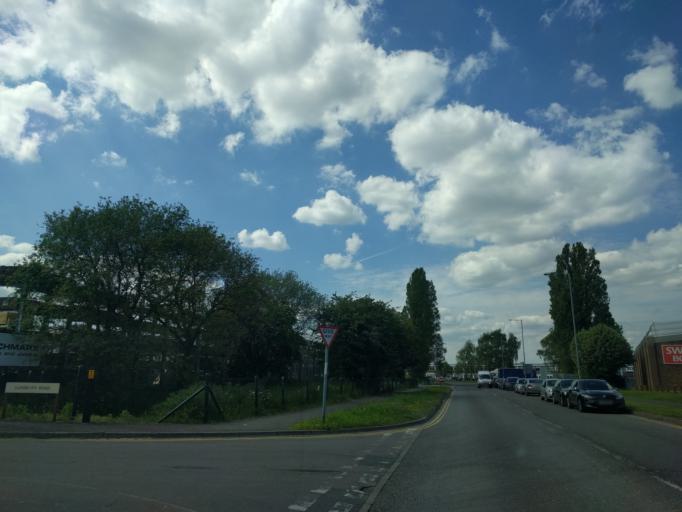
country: GB
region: England
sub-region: Borough of Swindon
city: Swindon
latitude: 51.5746
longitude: -1.7668
